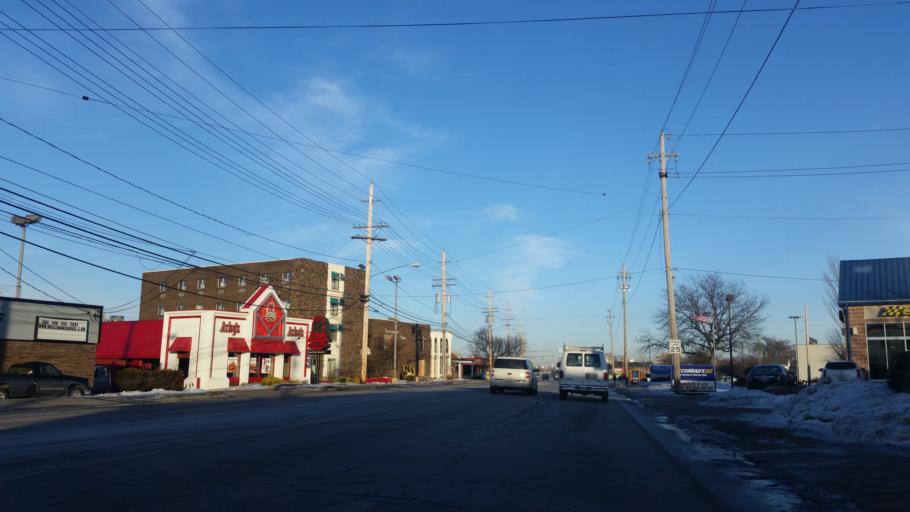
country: US
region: Ohio
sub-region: Cuyahoga County
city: Fairview Park
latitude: 41.4602
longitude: -81.8577
